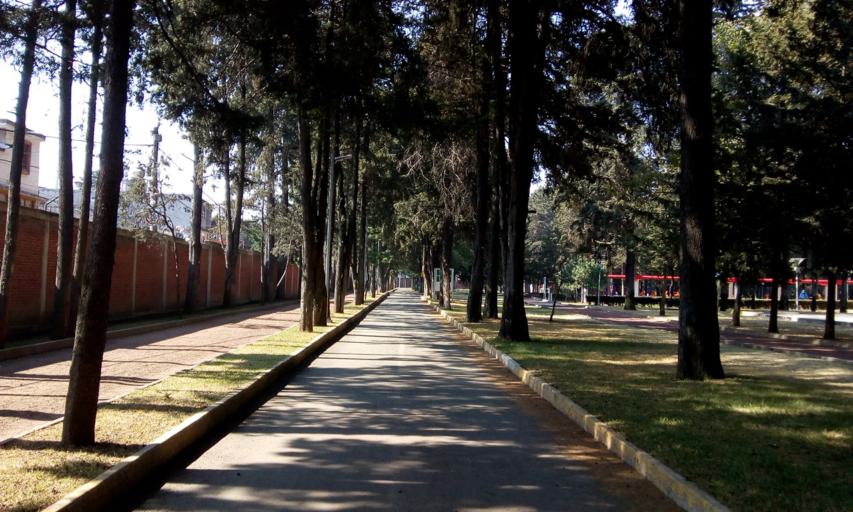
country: MX
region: Mexico
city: Toluca
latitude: 19.2709
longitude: -99.6493
